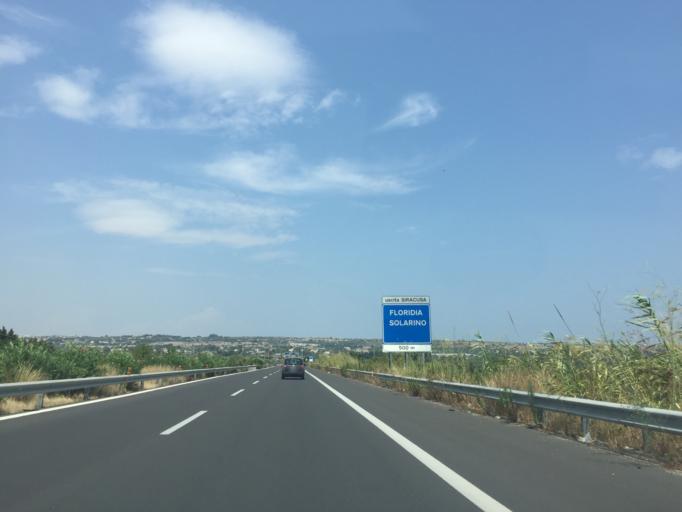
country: IT
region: Sicily
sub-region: Provincia di Siracusa
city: Belvedere
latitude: 37.0638
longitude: 15.2261
